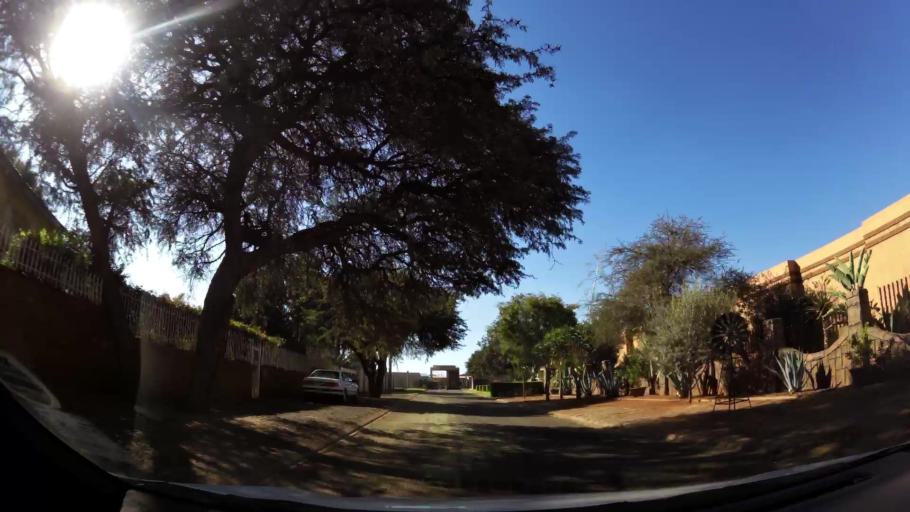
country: ZA
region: Limpopo
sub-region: Waterberg District Municipality
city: Mokopane
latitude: -24.2078
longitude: 28.9926
